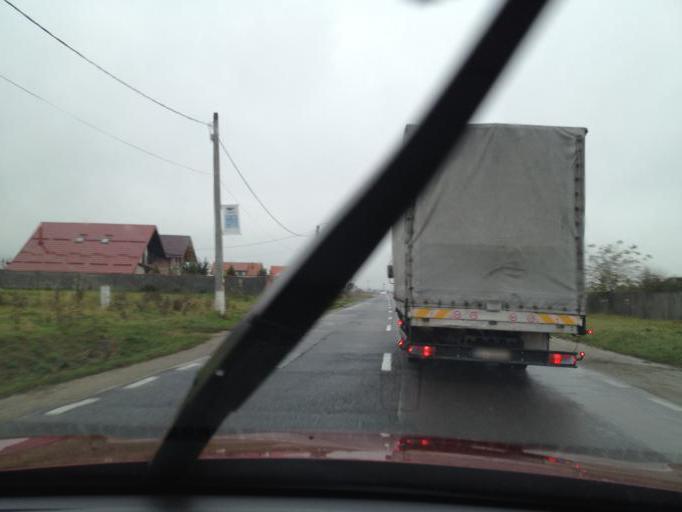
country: RO
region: Brasov
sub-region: Oras Rasnov
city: Rasnov
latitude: 45.5835
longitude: 25.4505
